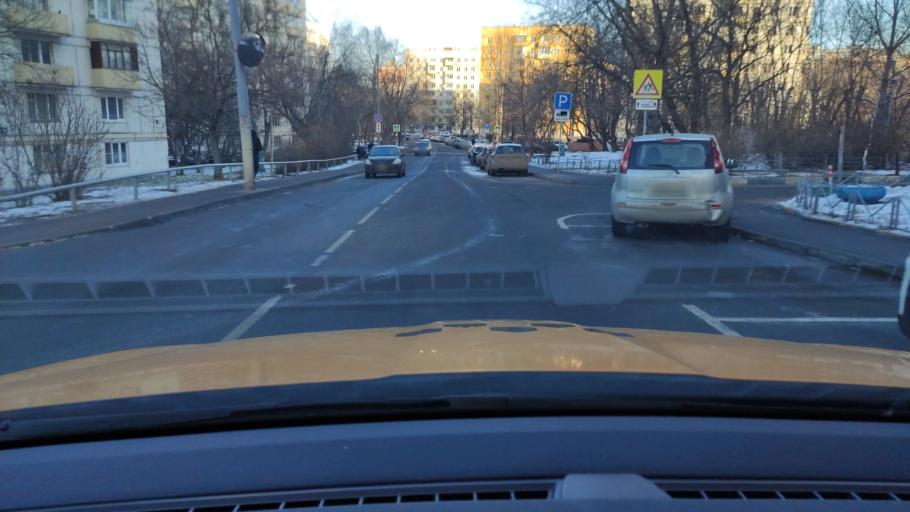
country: RU
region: Moskovskaya
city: Kozhukhovo
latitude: 55.6806
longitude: 37.6576
